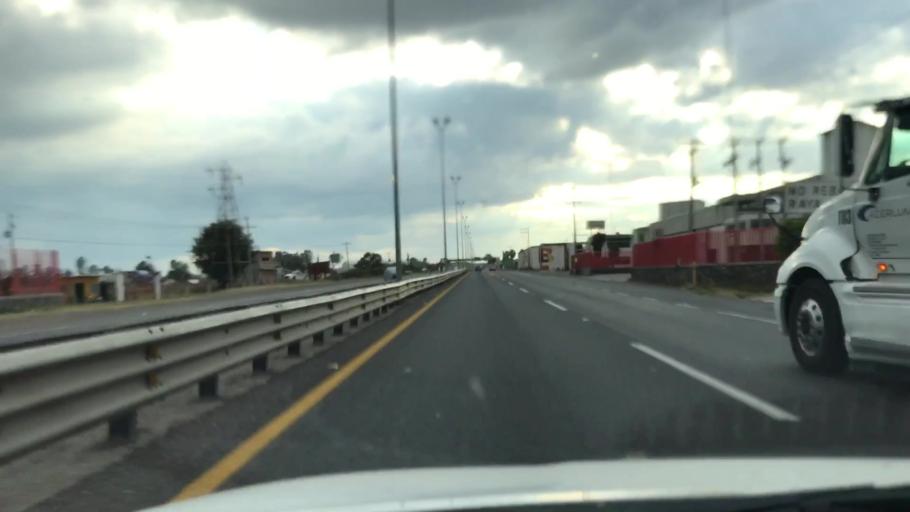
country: MX
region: Guanajuato
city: Penjamo
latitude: 20.4291
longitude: -101.7061
